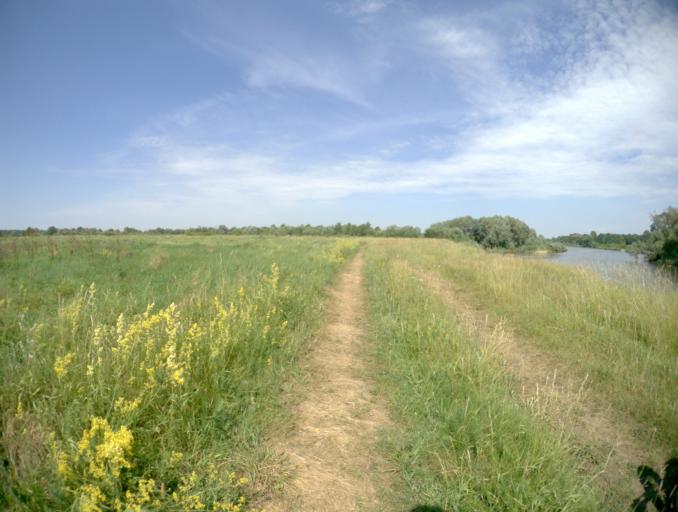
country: RU
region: Vladimir
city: Vorsha
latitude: 56.0356
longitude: 40.1798
